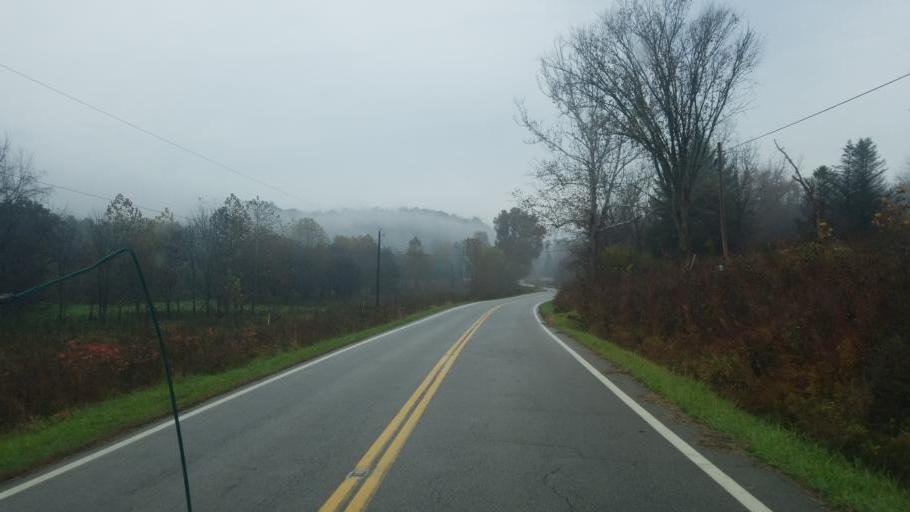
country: US
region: Ohio
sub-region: Athens County
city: Glouster
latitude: 39.4377
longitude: -81.9108
